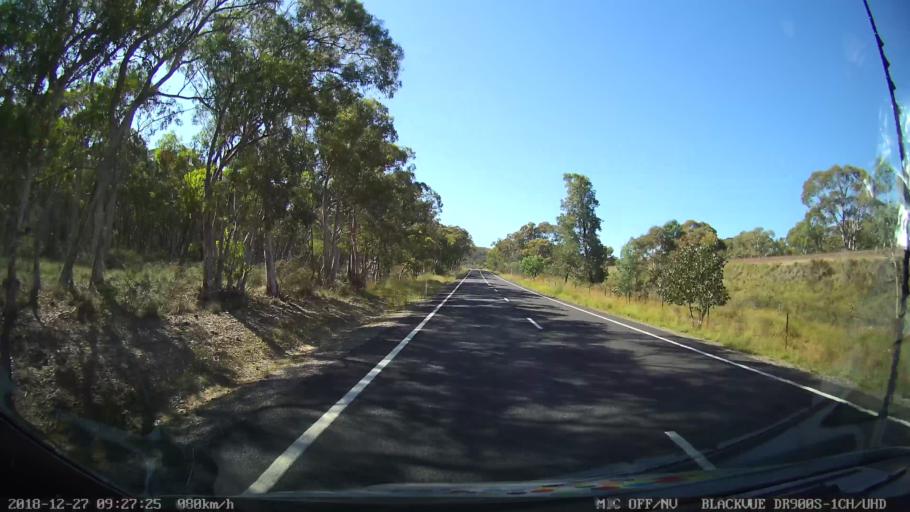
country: AU
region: New South Wales
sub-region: Lithgow
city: Portland
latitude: -33.1525
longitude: 149.9934
